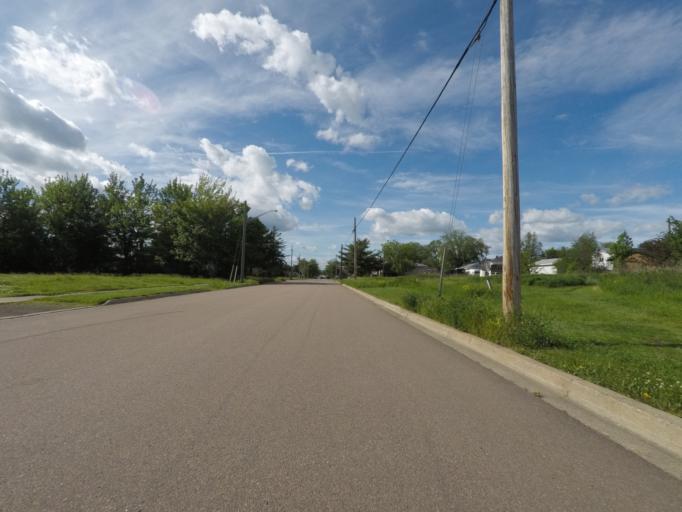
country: CA
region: New Brunswick
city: Moncton
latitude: 46.1003
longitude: -64.8232
